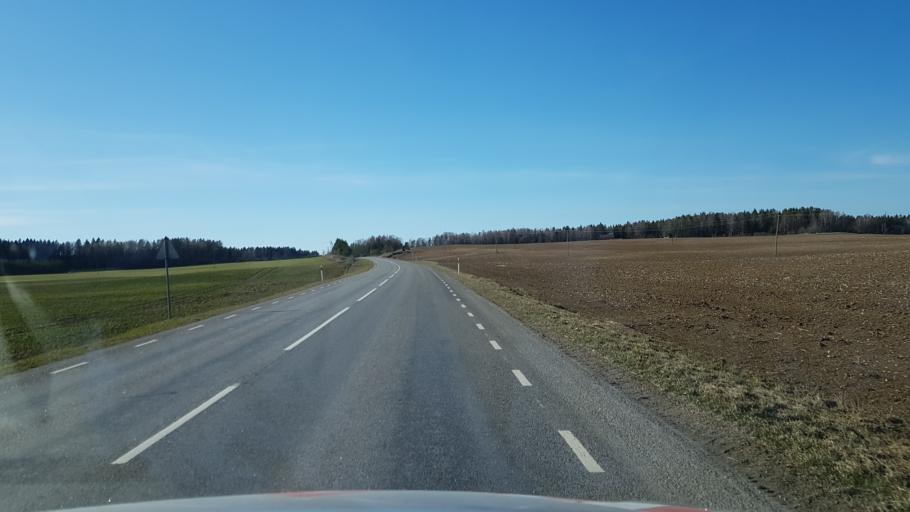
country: EE
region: Laeaene-Virumaa
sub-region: Vinni vald
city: Vinni
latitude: 59.3235
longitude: 26.4301
